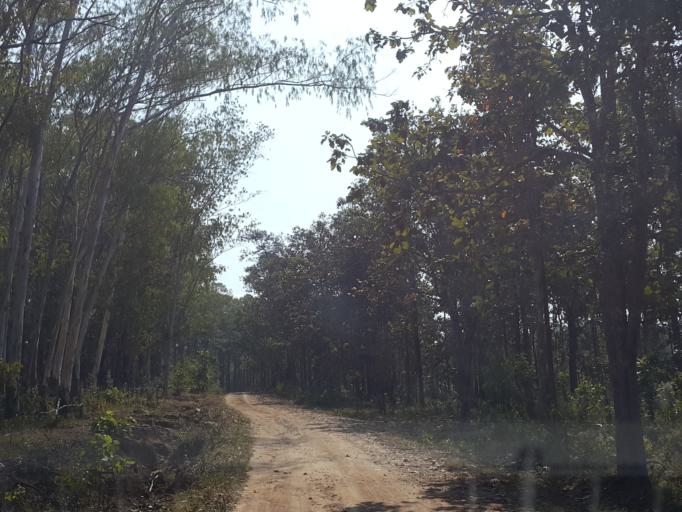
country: TH
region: Chiang Mai
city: Hot
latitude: 18.1494
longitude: 98.4312
